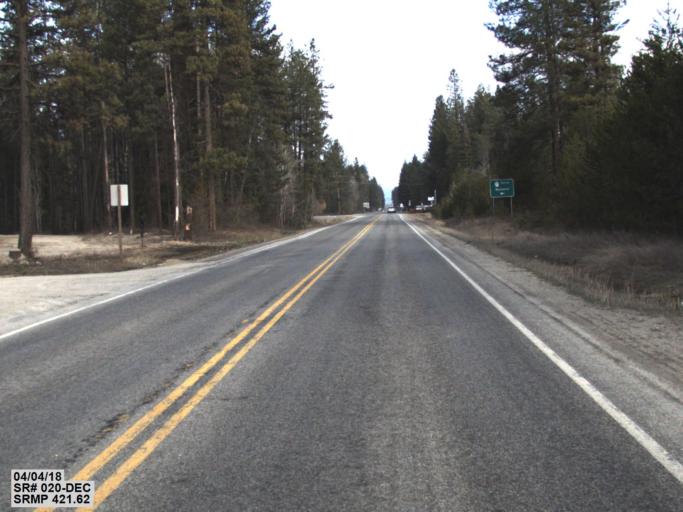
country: US
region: Washington
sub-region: Pend Oreille County
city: Newport
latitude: 48.3033
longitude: -117.2826
